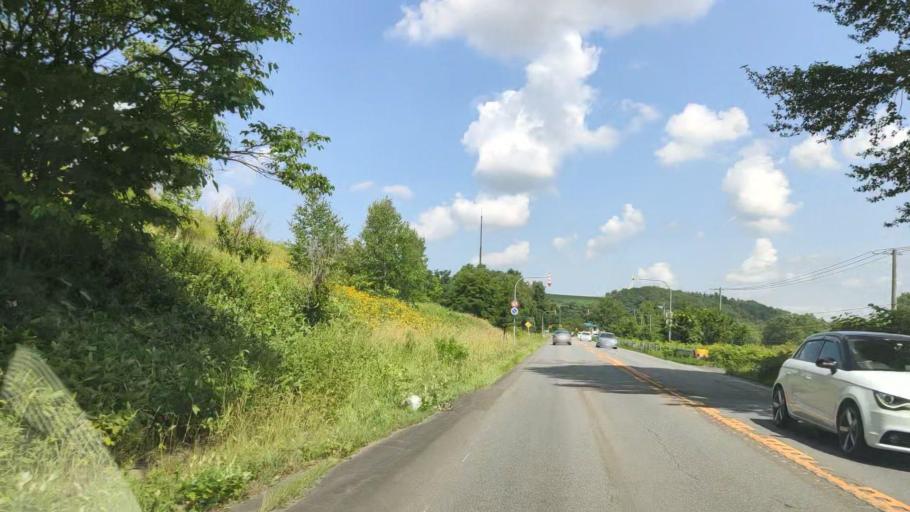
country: JP
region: Hokkaido
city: Shimo-furano
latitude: 43.5629
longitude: 142.4348
